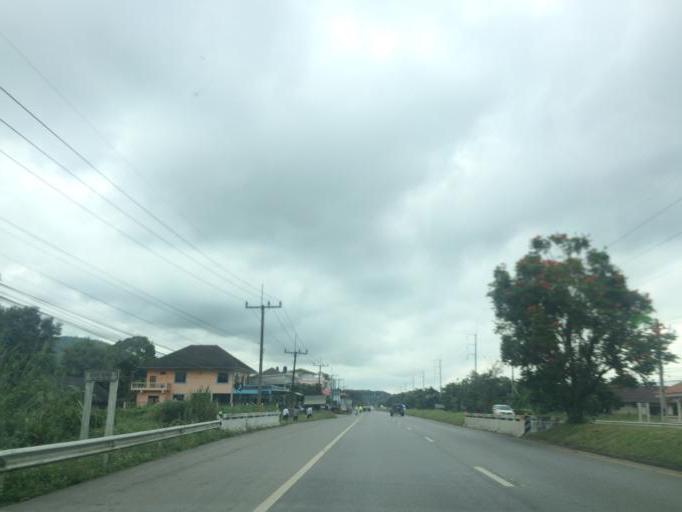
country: TH
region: Chiang Rai
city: Mae Chan
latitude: 20.0954
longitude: 99.8746
